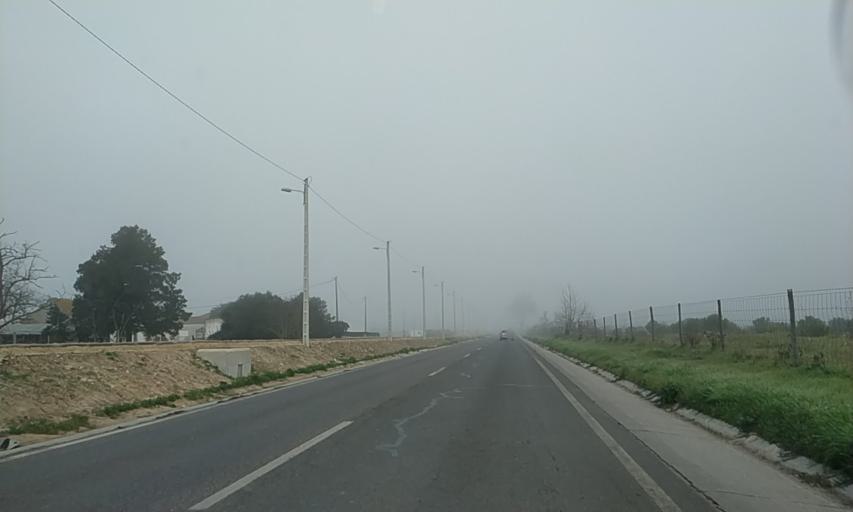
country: PT
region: Setubal
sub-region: Palmela
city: Pinhal Novo
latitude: 38.6434
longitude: -8.9149
